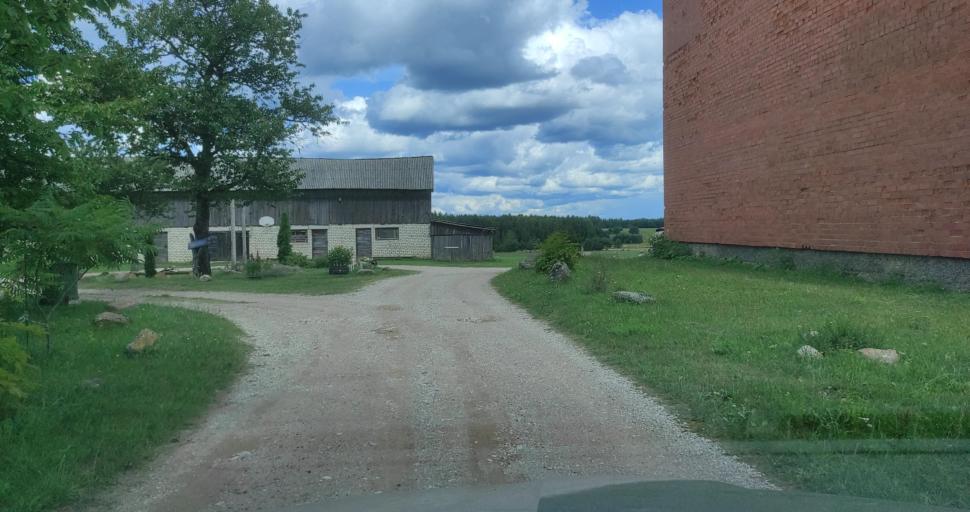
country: LV
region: Kuldigas Rajons
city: Kuldiga
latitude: 56.9894
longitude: 21.7934
